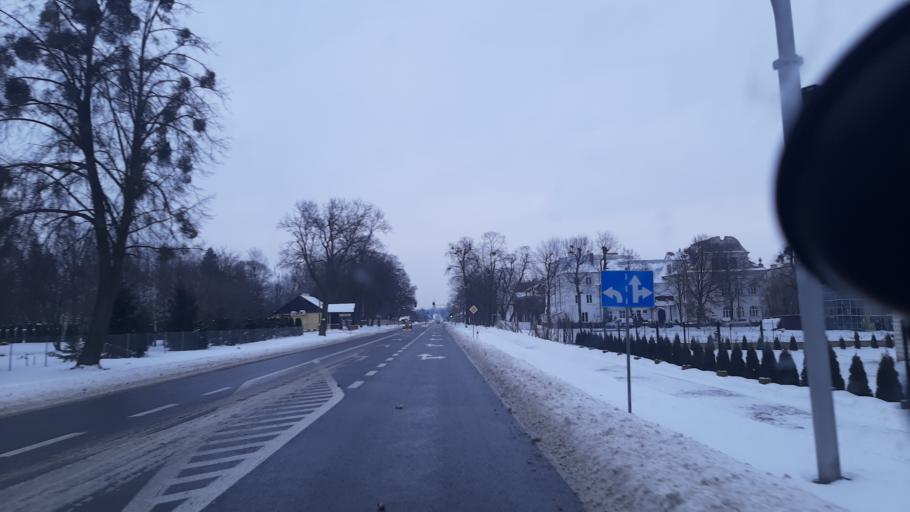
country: PL
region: Lublin Voivodeship
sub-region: Powiat lubelski
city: Garbow
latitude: 51.3652
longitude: 22.2947
